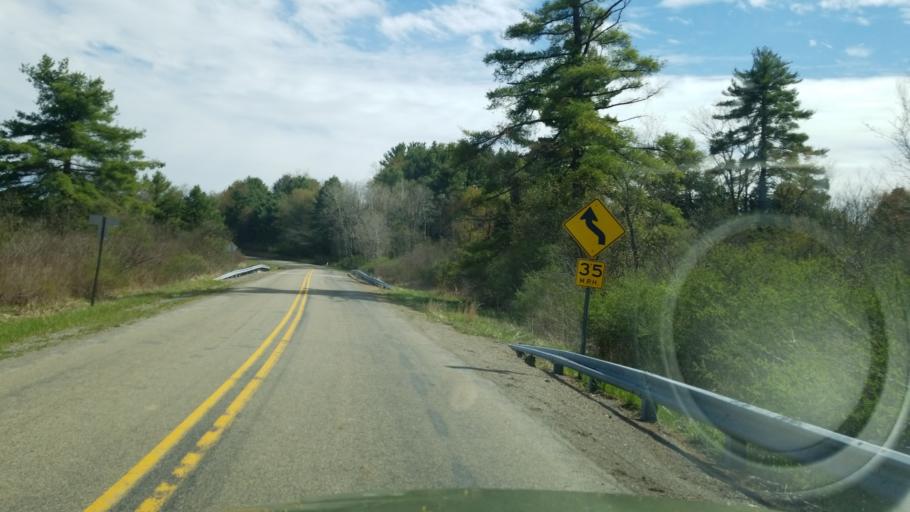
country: US
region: Pennsylvania
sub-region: Jefferson County
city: Brockway
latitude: 41.2328
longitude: -78.8516
